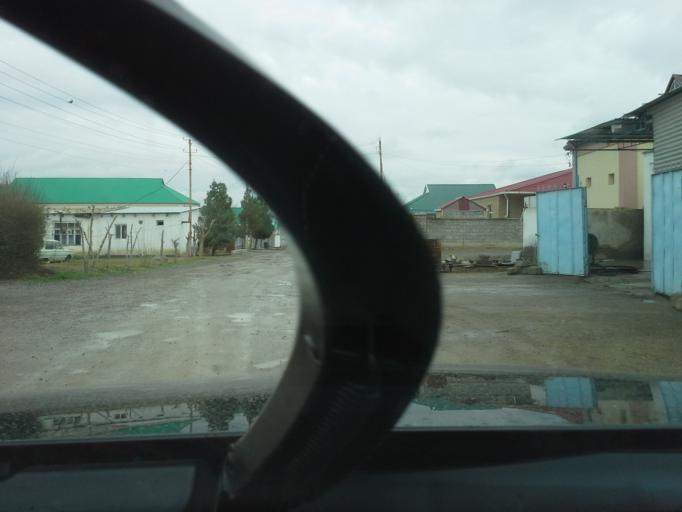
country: TM
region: Ahal
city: Abadan
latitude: 37.9702
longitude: 58.2066
